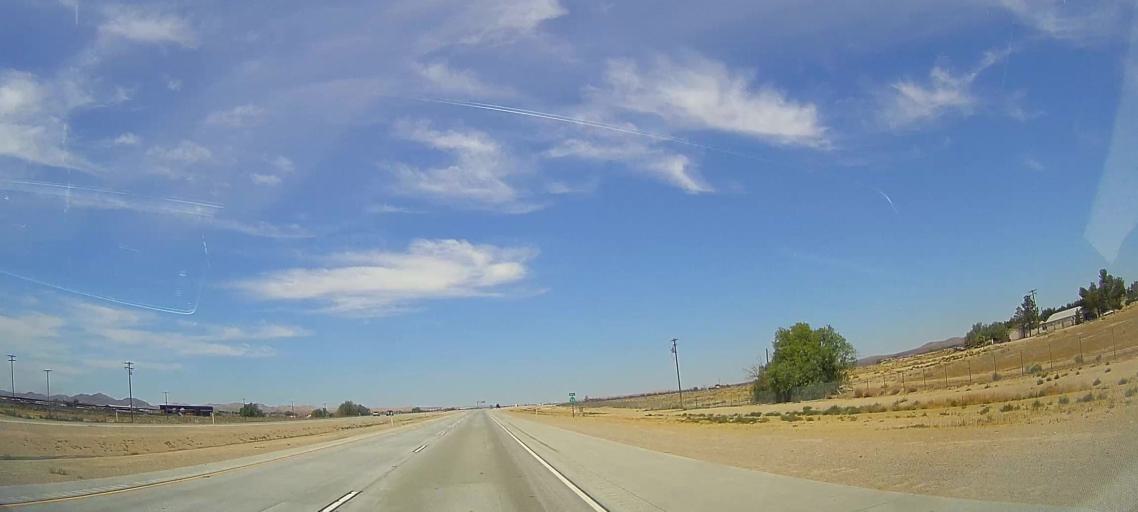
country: US
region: California
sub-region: San Bernardino County
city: Lenwood
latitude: 34.9158
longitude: -117.1356
